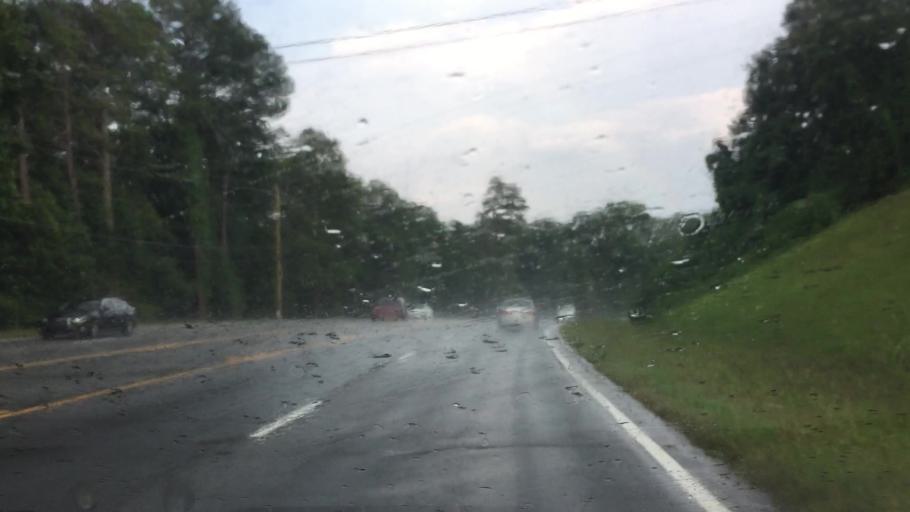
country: US
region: Georgia
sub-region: DeKalb County
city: Panthersville
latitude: 33.6832
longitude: -84.1979
